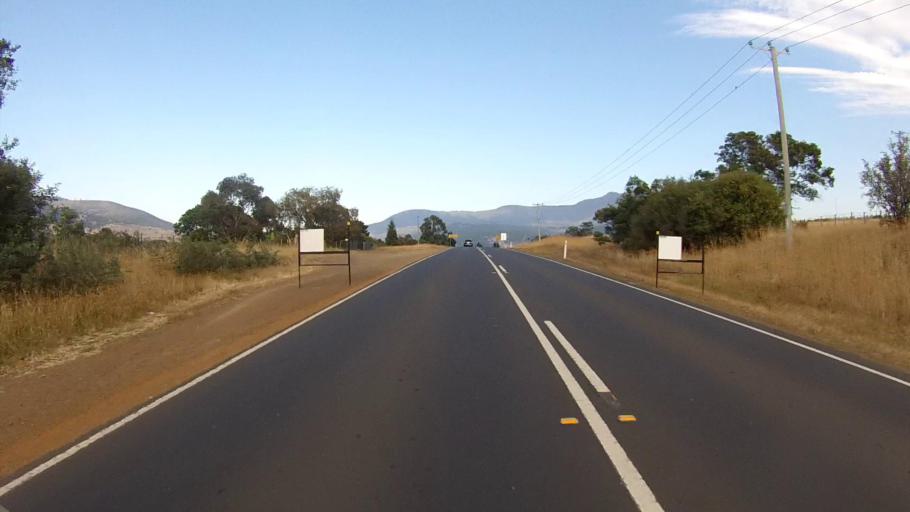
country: AU
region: Tasmania
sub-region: Brighton
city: Bridgewater
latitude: -42.7362
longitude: 147.2173
